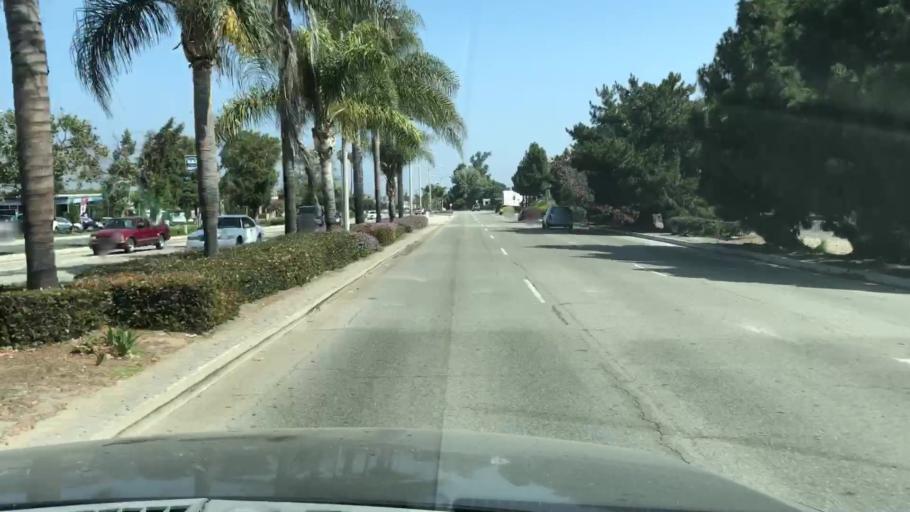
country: US
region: California
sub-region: Ventura County
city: El Rio
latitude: 34.2228
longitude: -119.1770
